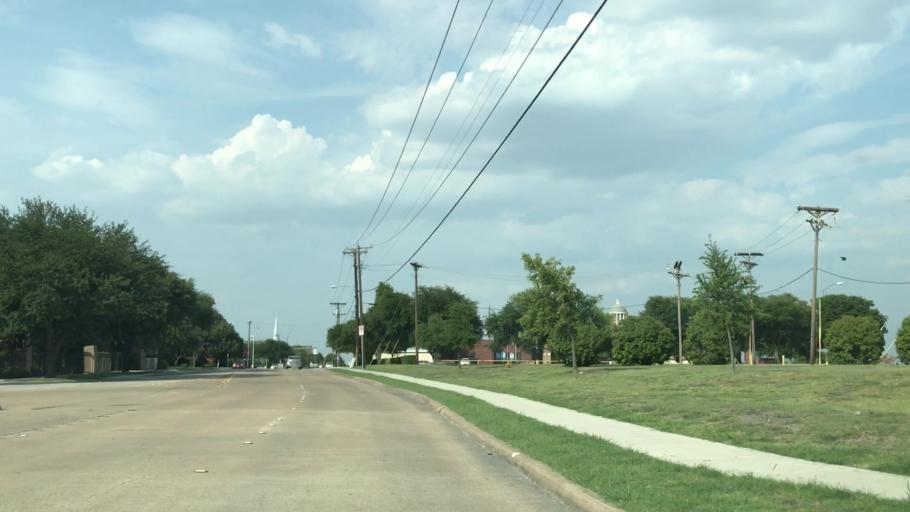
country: US
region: Texas
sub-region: Rockwall County
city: Rockwall
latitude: 32.9109
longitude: -96.4544
